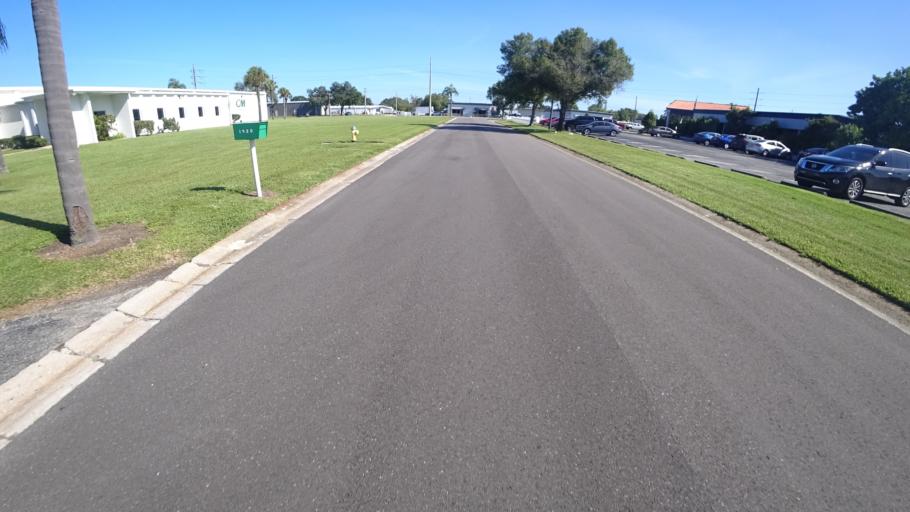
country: US
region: Florida
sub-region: Manatee County
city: Whitfield
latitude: 27.4172
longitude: -82.5396
